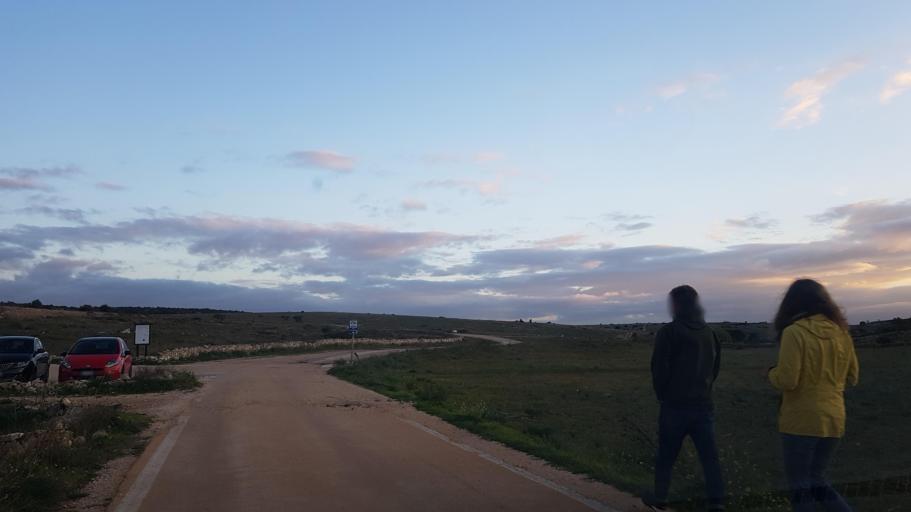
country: IT
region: Basilicate
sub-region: Provincia di Matera
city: Matera
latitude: 40.6723
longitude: 16.6284
